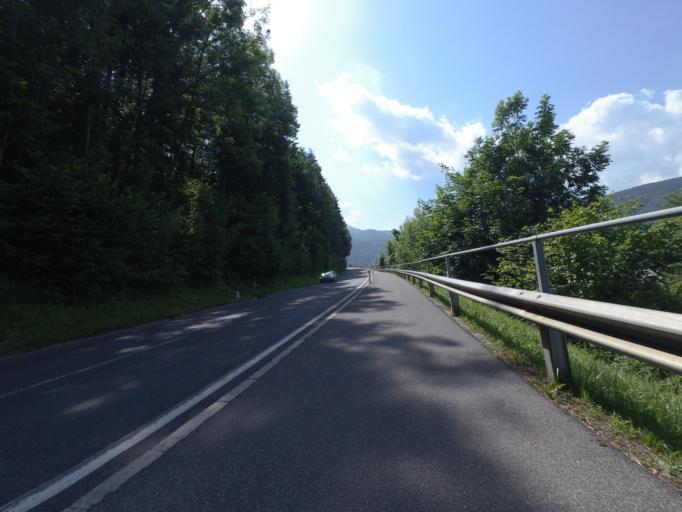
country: AT
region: Carinthia
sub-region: Politischer Bezirk Villach Land
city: Ferndorf
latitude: 46.7778
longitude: 13.6298
